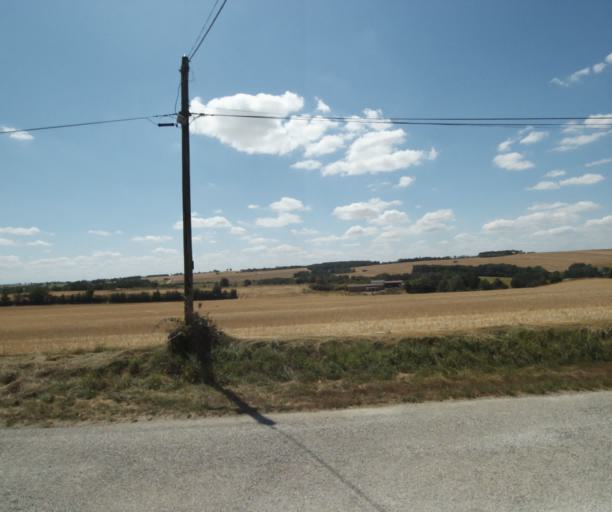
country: FR
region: Midi-Pyrenees
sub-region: Departement de la Haute-Garonne
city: Auriac-sur-Vendinelle
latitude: 43.5061
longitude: 1.8399
